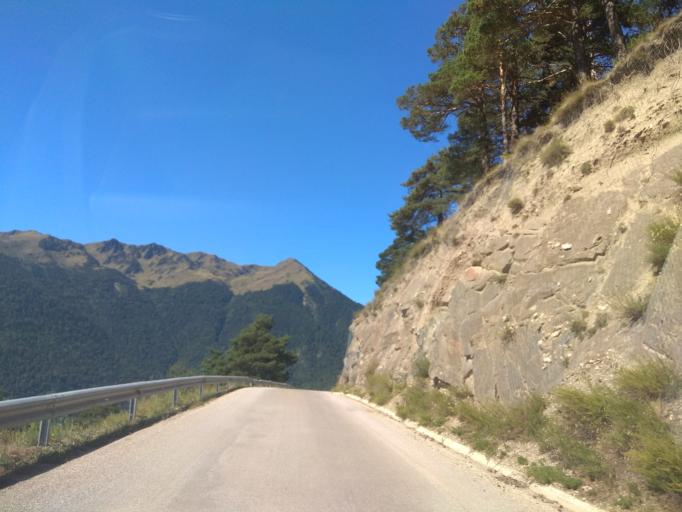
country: ES
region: Catalonia
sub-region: Provincia de Lleida
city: Les
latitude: 42.7500
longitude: 0.7173
